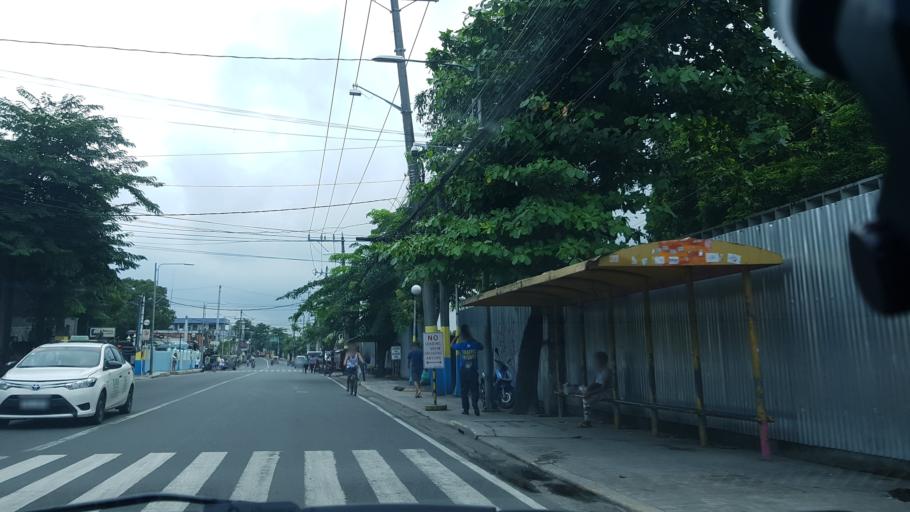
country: PH
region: Calabarzon
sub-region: Province of Rizal
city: Pateros
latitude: 14.5512
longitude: 121.0742
